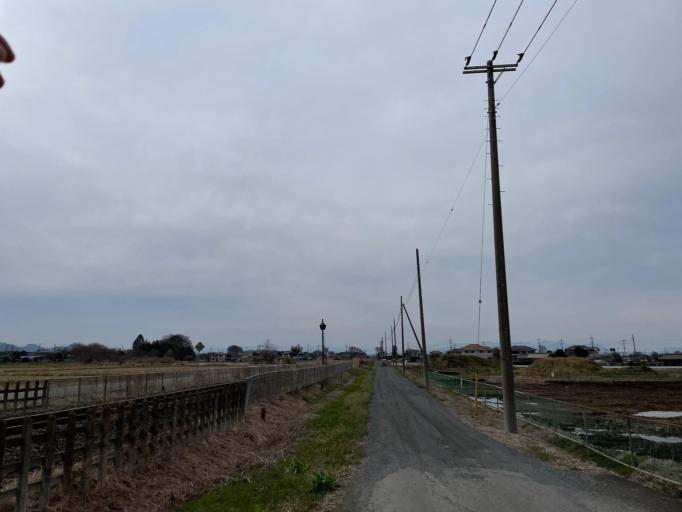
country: JP
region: Saitama
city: Kodamacho-kodamaminami
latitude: 36.2034
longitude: 139.1223
